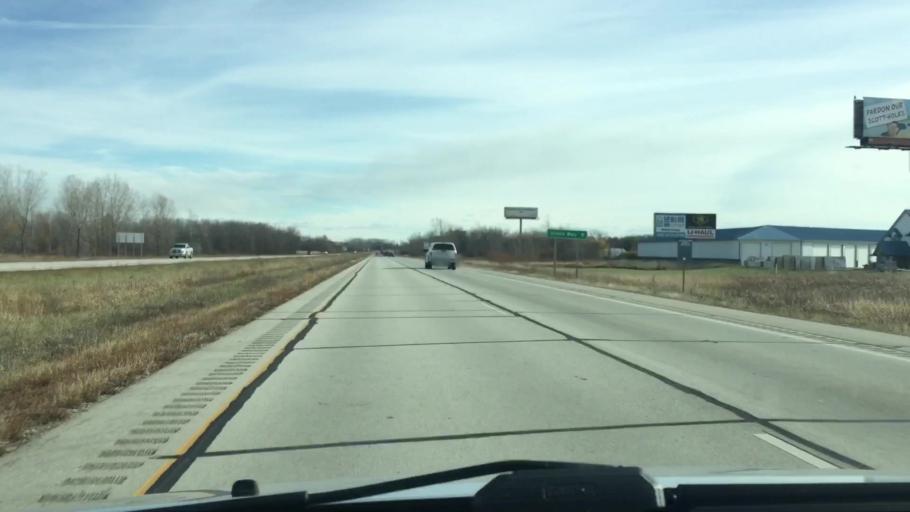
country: US
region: Wisconsin
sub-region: Brown County
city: Pulaski
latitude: 44.5929
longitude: -88.2098
